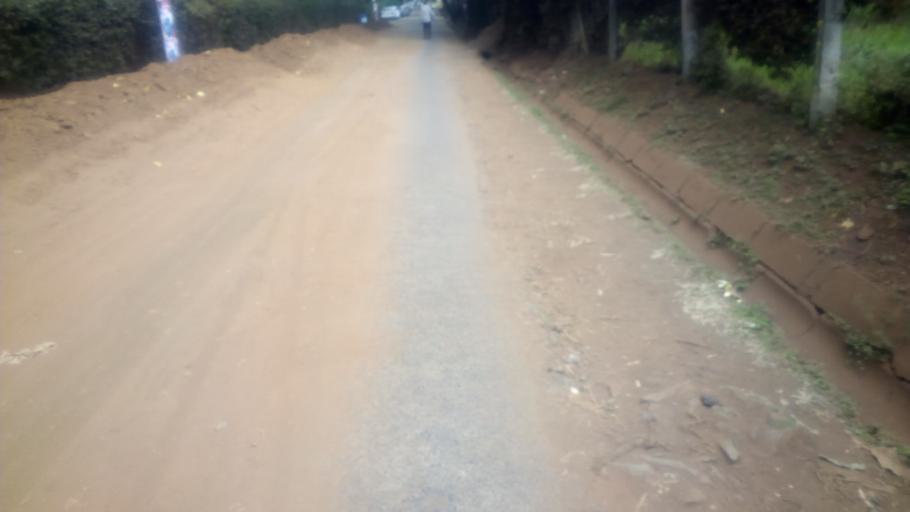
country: KE
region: Nairobi Area
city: Nairobi
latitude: -1.2802
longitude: 36.8102
